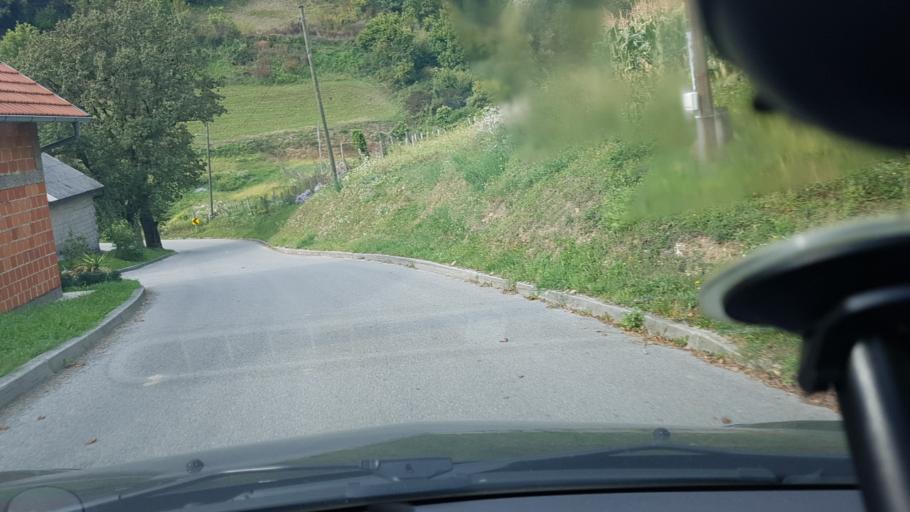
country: HR
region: Krapinsko-Zagorska
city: Radoboj
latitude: 46.1724
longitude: 15.9451
